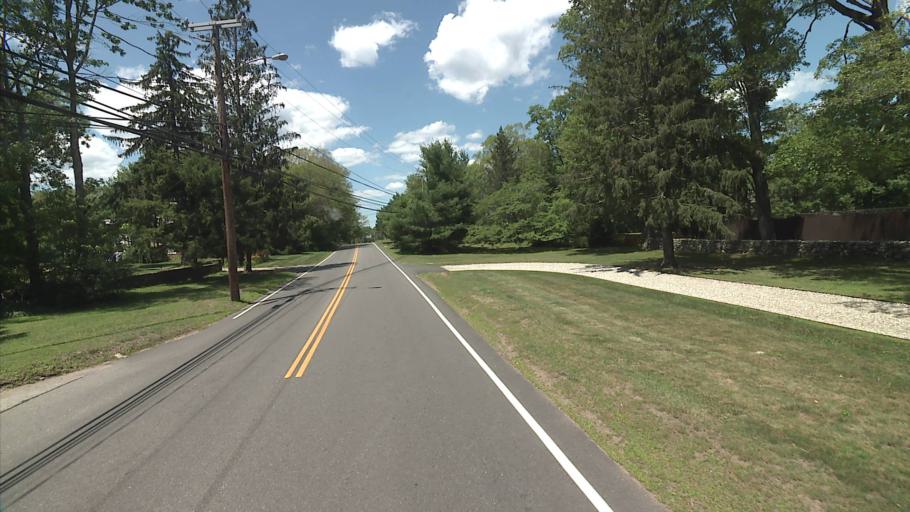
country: US
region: Connecticut
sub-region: Middlesex County
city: Moodus
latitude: 41.4770
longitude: -72.4452
